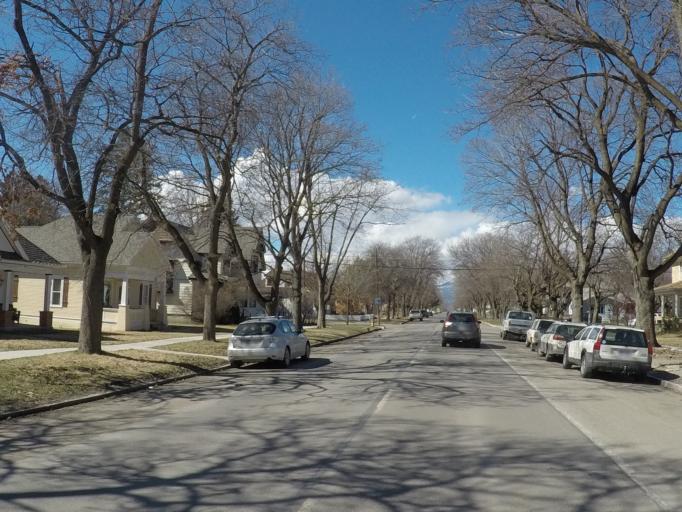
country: US
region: Montana
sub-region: Missoula County
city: Missoula
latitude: 46.8651
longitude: -114.0057
